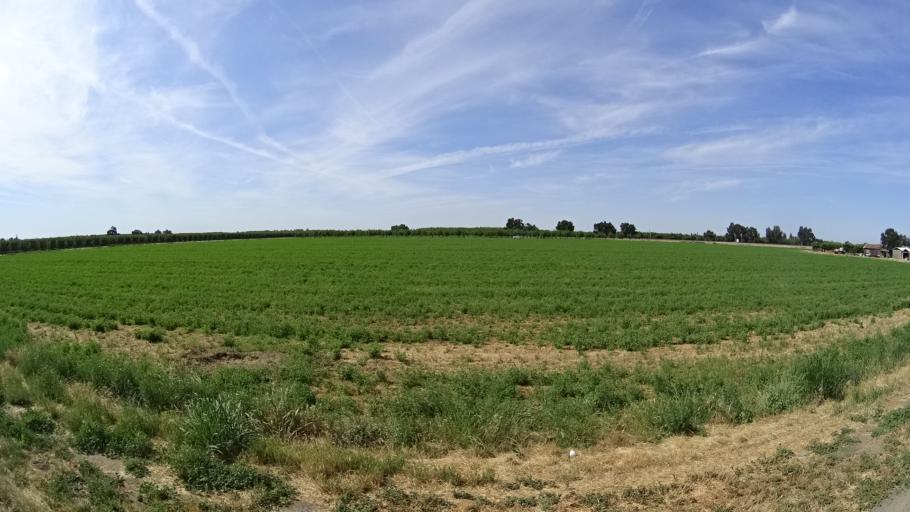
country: US
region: California
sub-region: Fresno County
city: Laton
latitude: 36.4158
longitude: -119.6652
